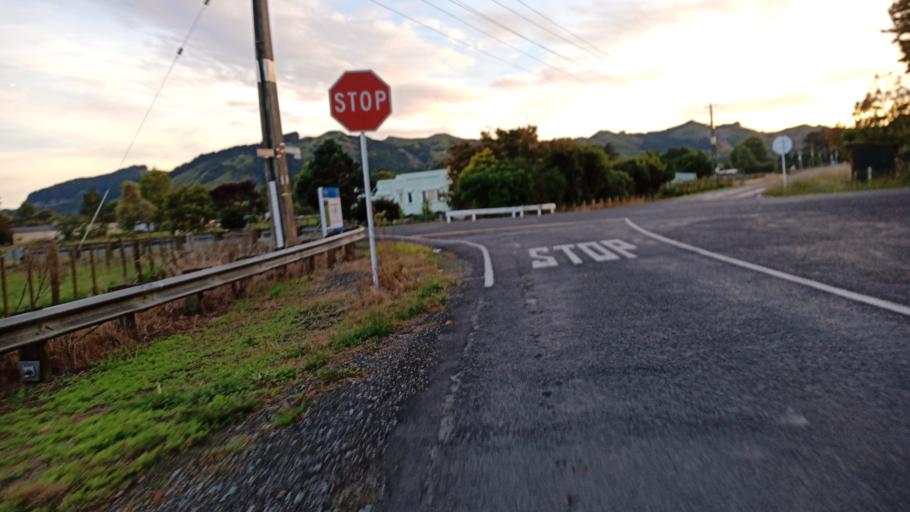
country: NZ
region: Gisborne
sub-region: Gisborne District
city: Gisborne
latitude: -38.6204
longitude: 177.9807
